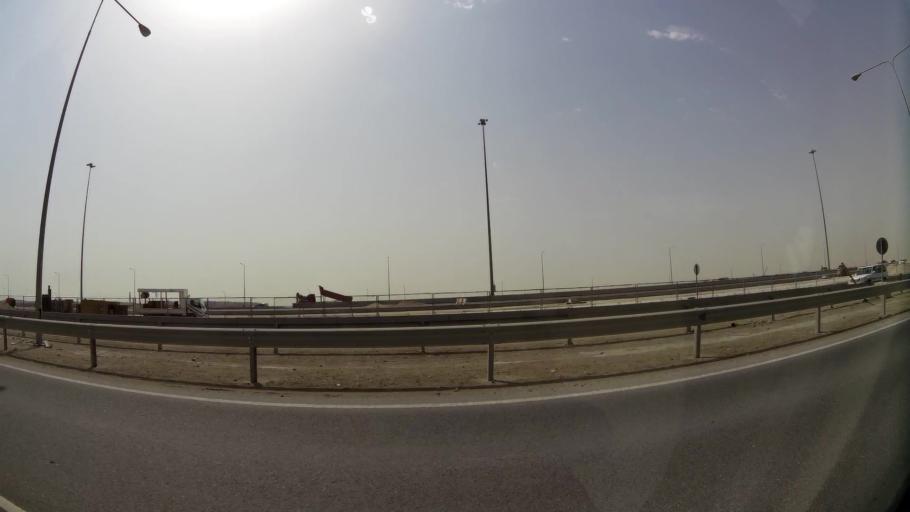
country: QA
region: Al Wakrah
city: Al Wukayr
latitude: 25.2050
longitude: 51.4834
